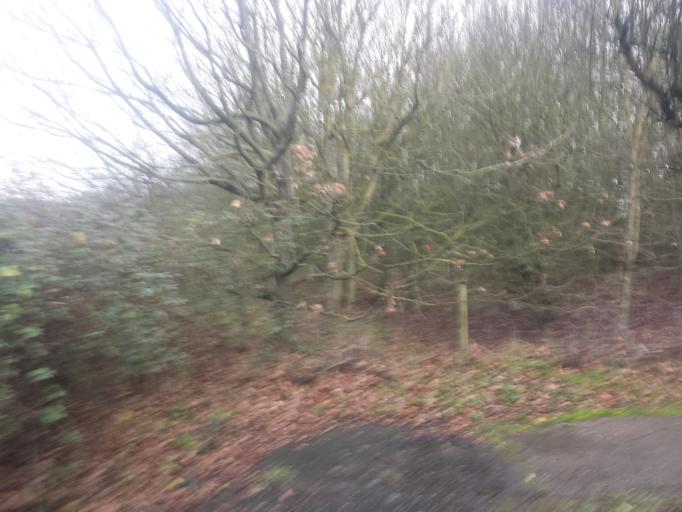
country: GB
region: England
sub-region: Essex
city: Great Bentley
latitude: 51.8859
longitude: 1.0450
